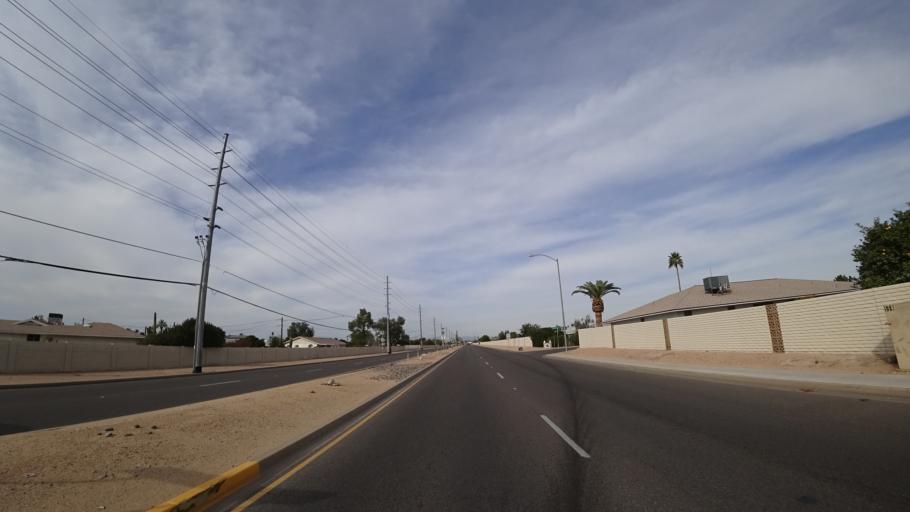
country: US
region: Arizona
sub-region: Maricopa County
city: Sun City
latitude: 33.5879
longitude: -112.2725
